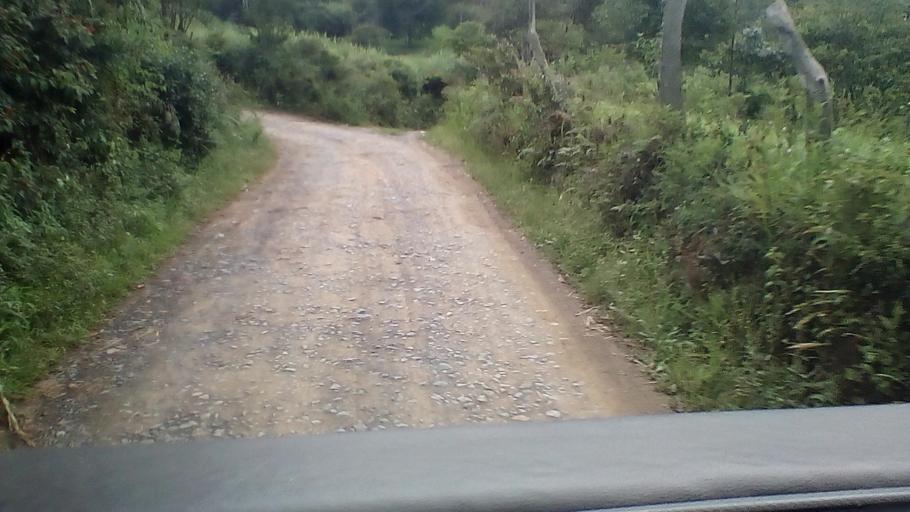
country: CO
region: Boyaca
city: Santana
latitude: 6.0181
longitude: -73.5126
